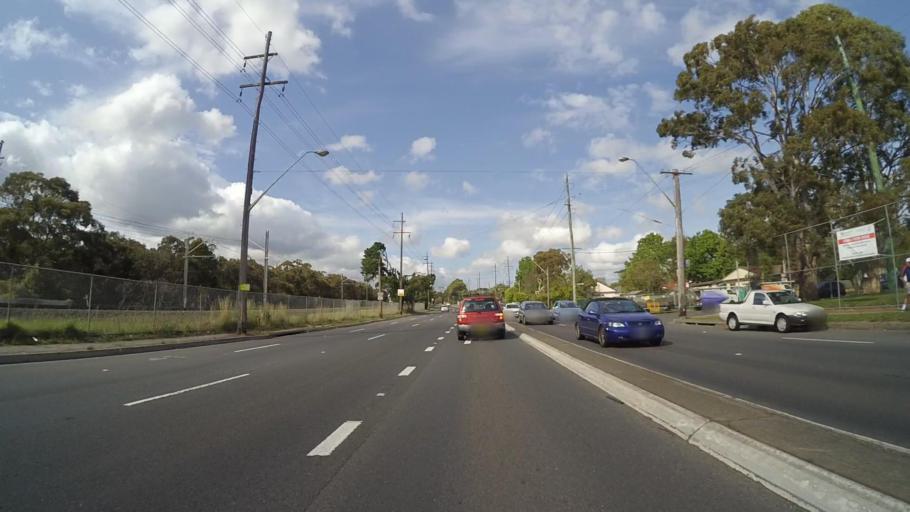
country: AU
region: New South Wales
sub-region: Sutherland Shire
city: Engadine
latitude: -34.0695
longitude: 151.0131
